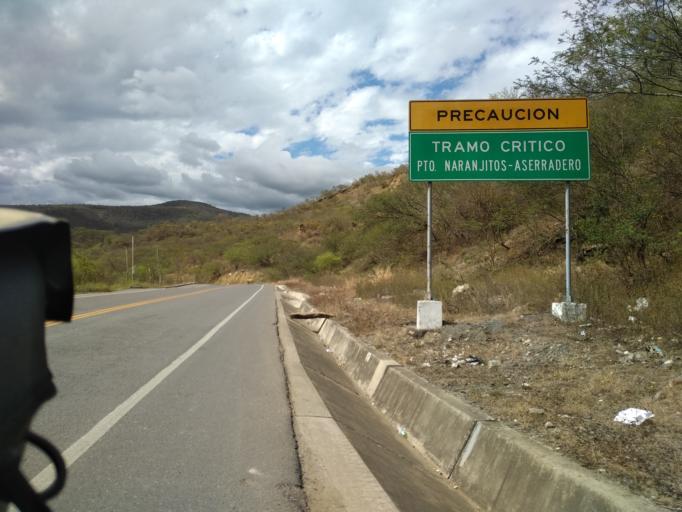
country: PE
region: Amazonas
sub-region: Utcubamba
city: Jamalca
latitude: -5.8227
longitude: -78.2744
